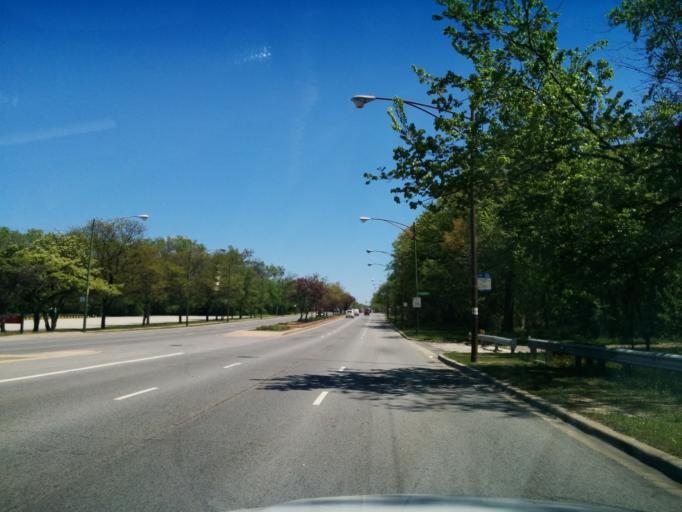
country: US
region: Illinois
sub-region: Cook County
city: Evergreen Park
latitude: 41.7355
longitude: -87.6766
